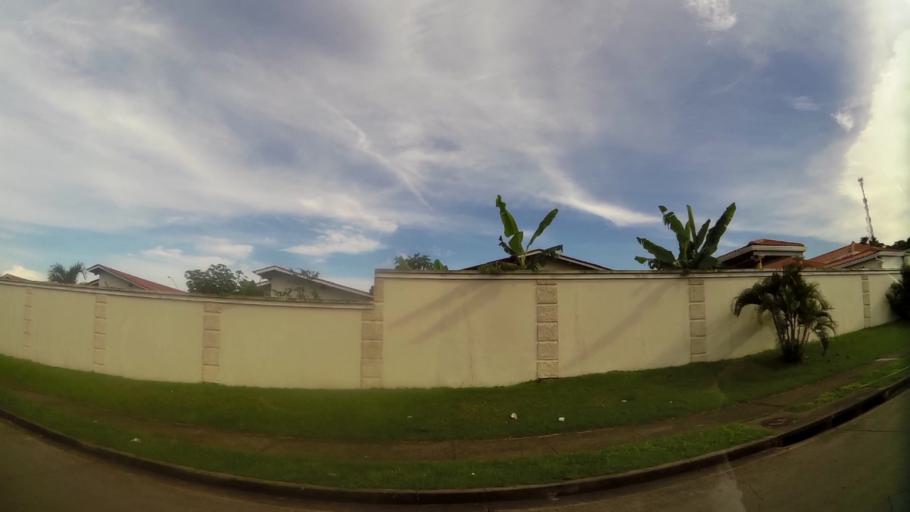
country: PA
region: Panama
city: La Chorrera
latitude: 8.8802
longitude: -79.7633
